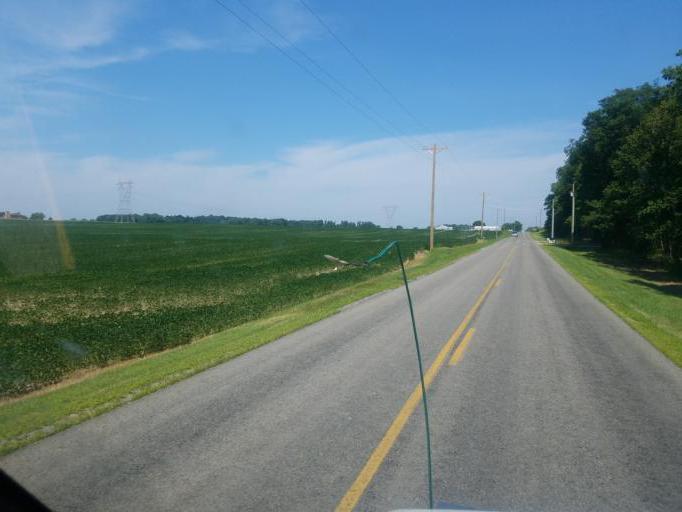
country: US
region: Ohio
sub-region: Shelby County
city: Jackson Center
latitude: 40.4976
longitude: -84.0847
